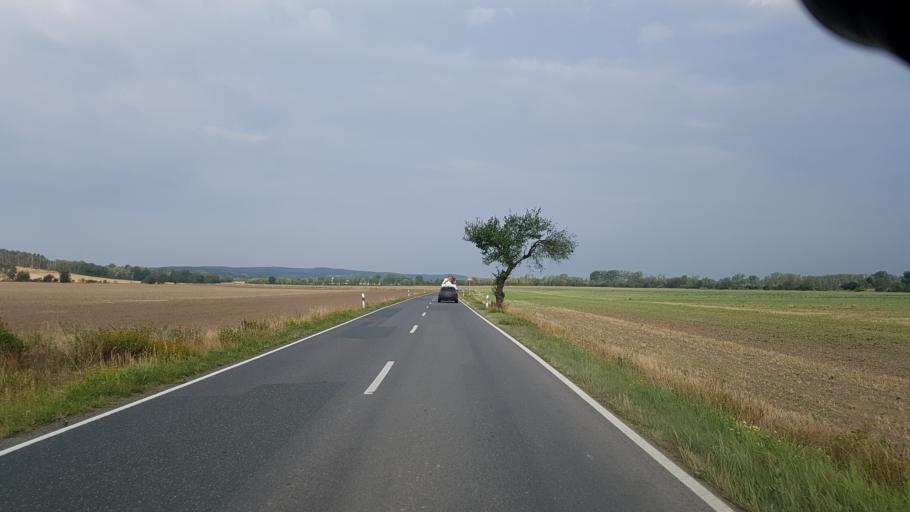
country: DE
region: Brandenburg
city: Grossthiemig
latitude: 51.3857
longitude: 13.6647
